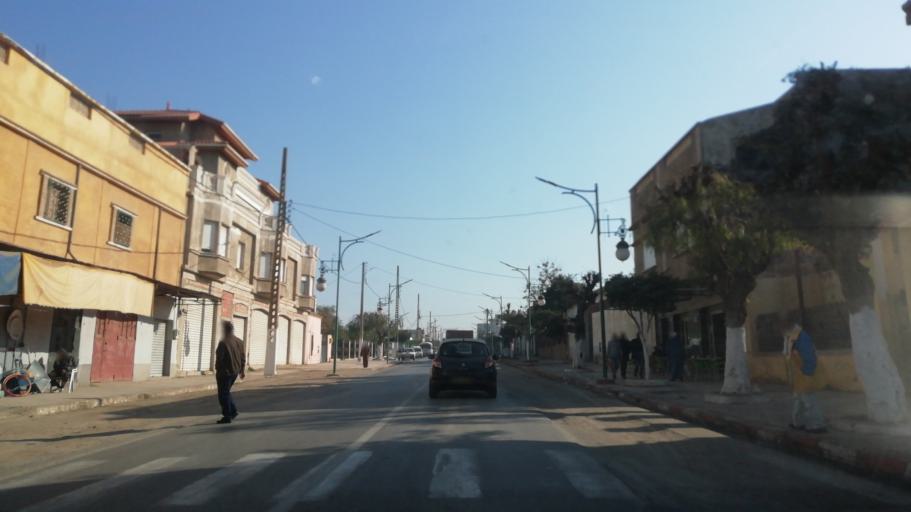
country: DZ
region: Relizane
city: Relizane
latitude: 35.7334
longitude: 0.4577
